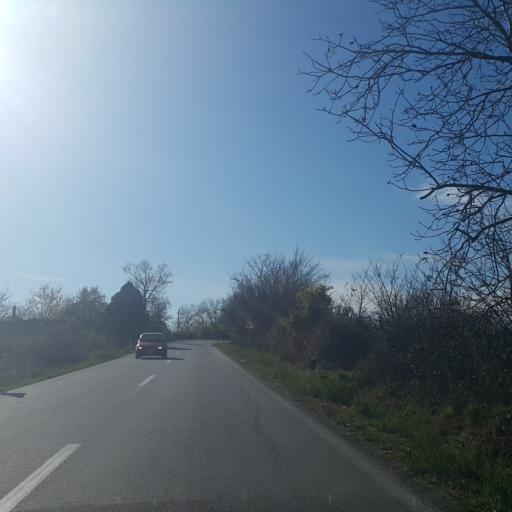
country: RS
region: Central Serbia
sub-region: Sumadijski Okrug
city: Topola
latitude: 44.2509
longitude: 20.7854
